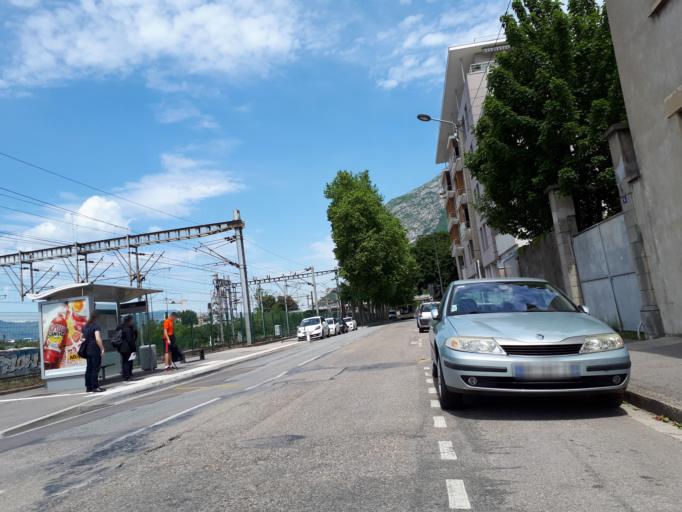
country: FR
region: Rhone-Alpes
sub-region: Departement de l'Isere
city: Saint-Martin-le-Vinoux
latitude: 45.1969
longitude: 5.7119
